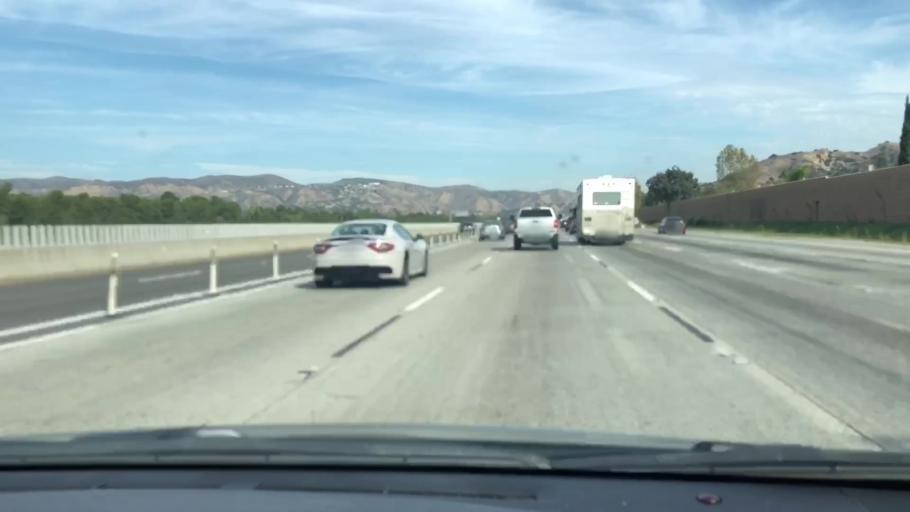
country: US
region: California
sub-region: Orange County
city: Yorba Linda
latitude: 33.8627
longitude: -117.7720
